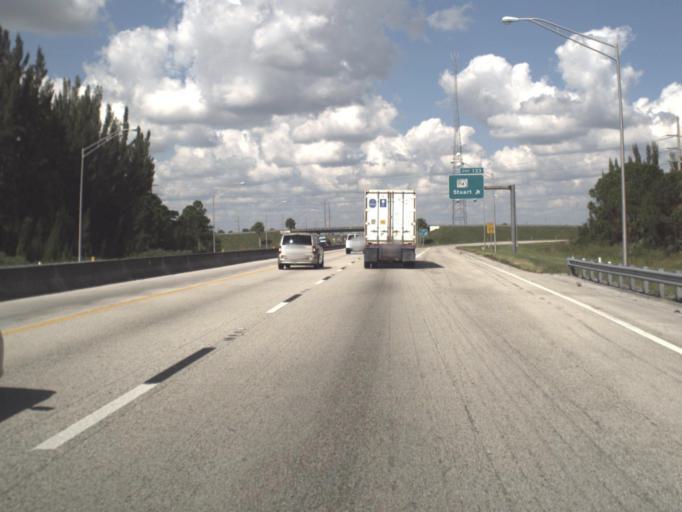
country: US
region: Florida
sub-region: Martin County
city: Palm City
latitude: 27.1550
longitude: -80.3002
